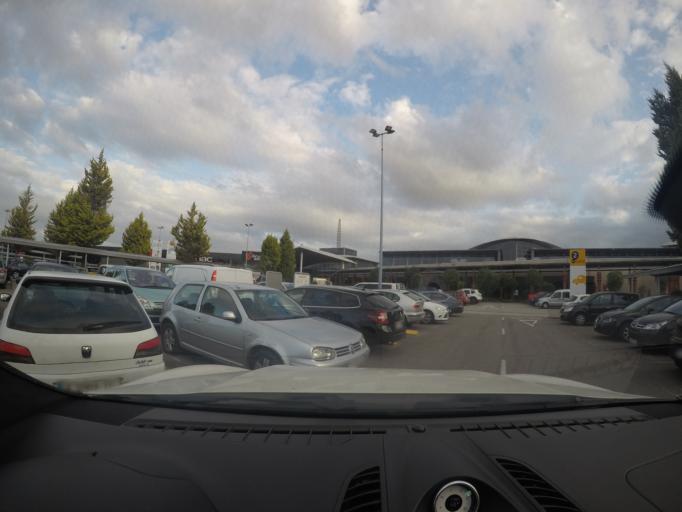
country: ES
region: Asturias
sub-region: Province of Asturias
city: Lugones
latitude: 43.3912
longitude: -5.8017
